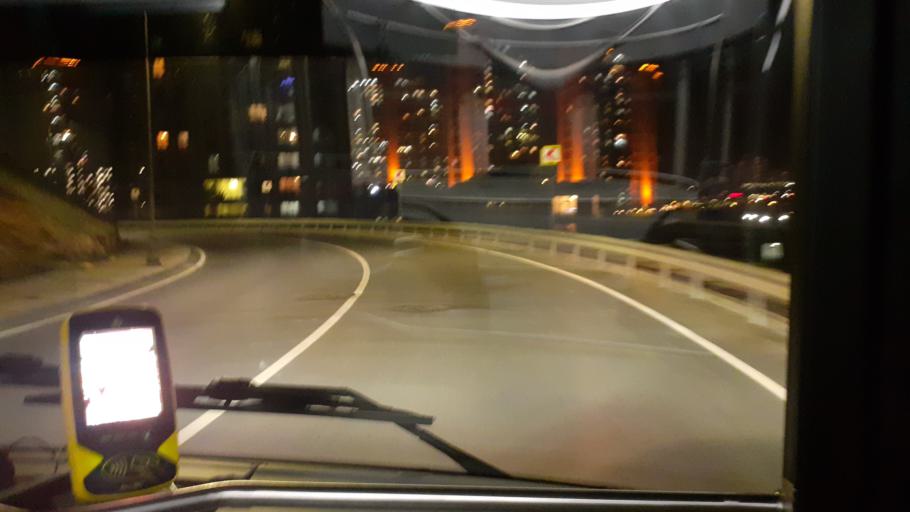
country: TR
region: Istanbul
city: Basaksehir
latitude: 41.0708
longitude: 28.7767
